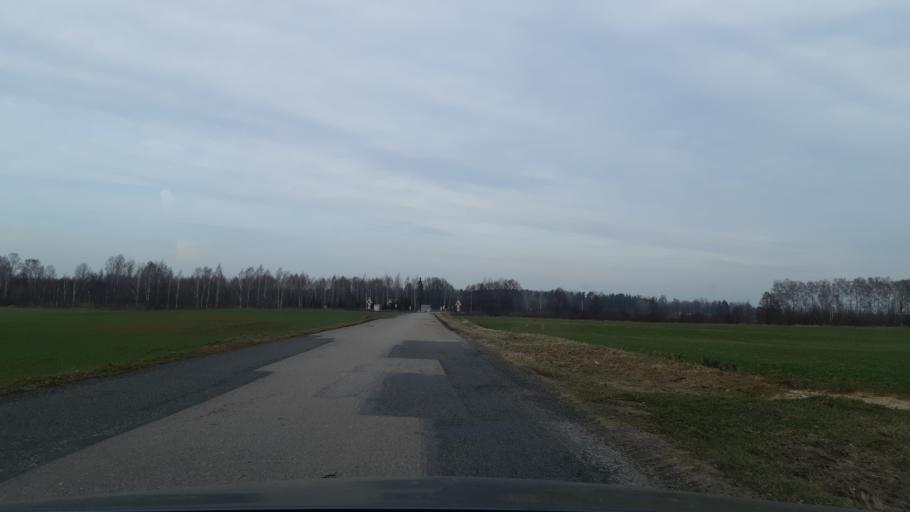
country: LT
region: Marijampoles apskritis
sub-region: Marijampole Municipality
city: Marijampole
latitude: 54.7242
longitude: 23.3369
